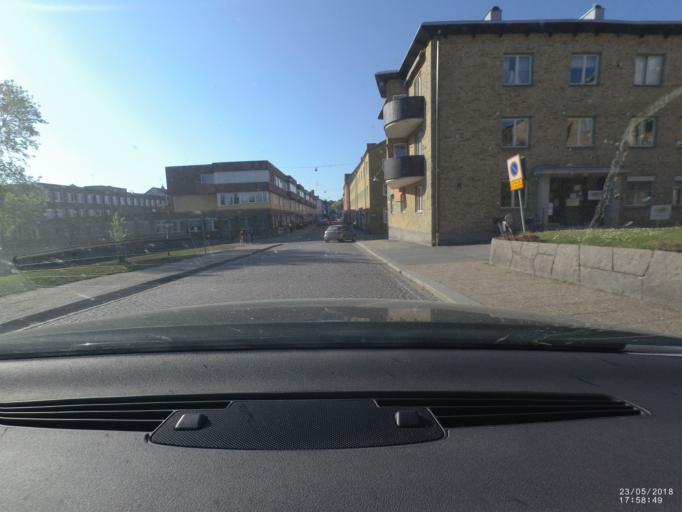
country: SE
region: Soedermanland
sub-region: Nykopings Kommun
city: Nykoping
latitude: 58.7533
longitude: 17.0160
